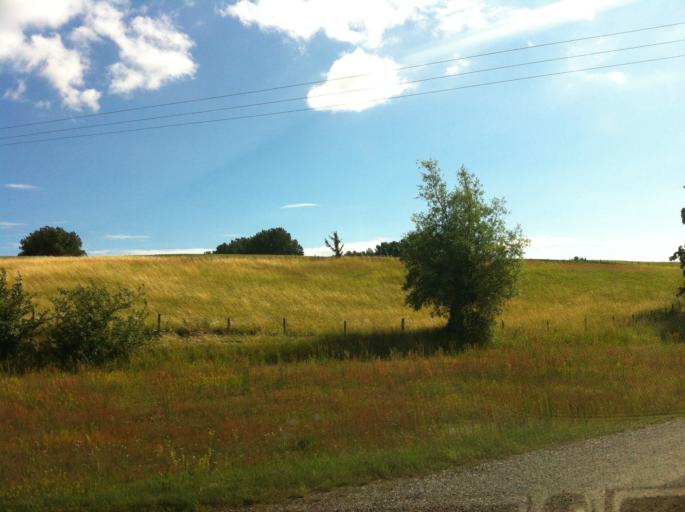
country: SE
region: Skane
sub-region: Ystads Kommun
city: Kopingebro
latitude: 55.3934
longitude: 14.0436
